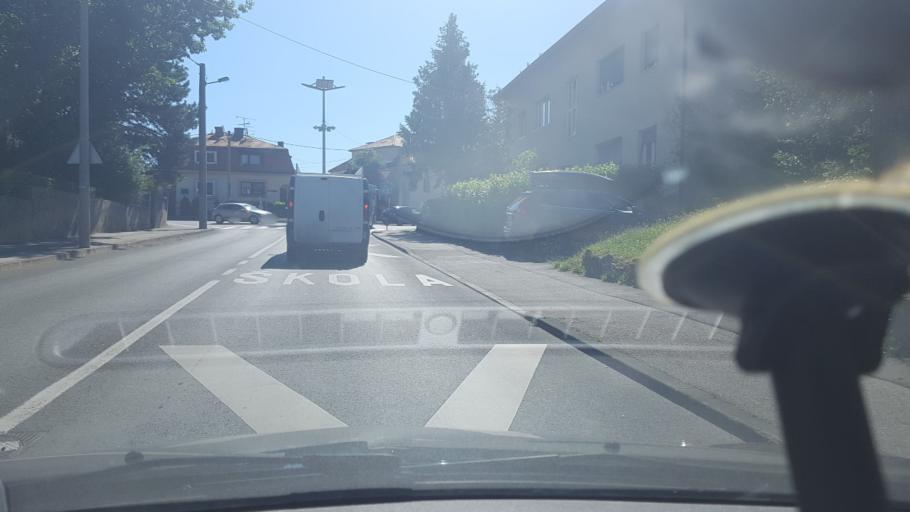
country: HR
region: Grad Zagreb
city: Zagreb
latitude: 45.8242
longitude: 15.9842
